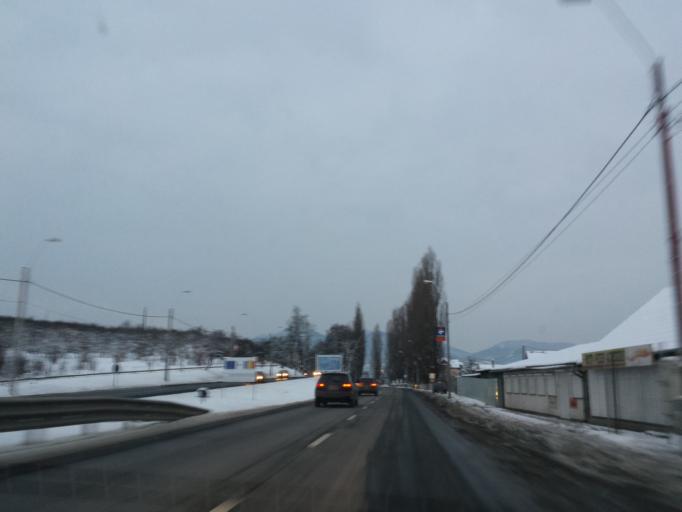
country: RO
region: Hunedoara
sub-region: Municipiul Deva
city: Cristur
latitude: 45.8596
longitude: 22.9359
